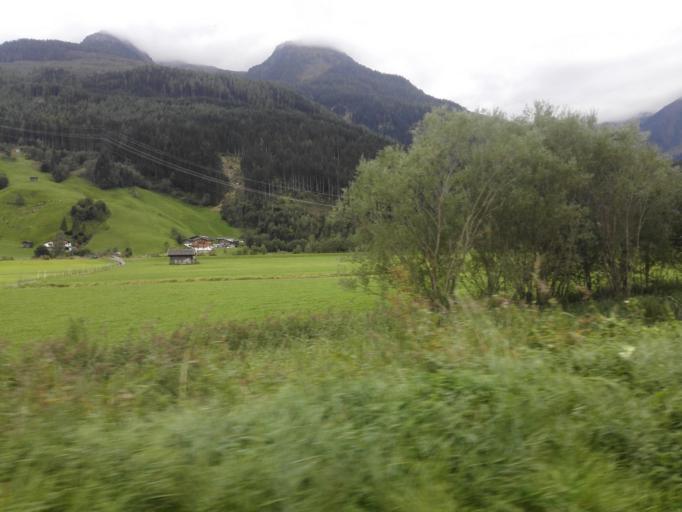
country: AT
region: Salzburg
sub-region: Politischer Bezirk Zell am See
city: Bramberg am Wildkogel
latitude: 47.2702
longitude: 12.3456
